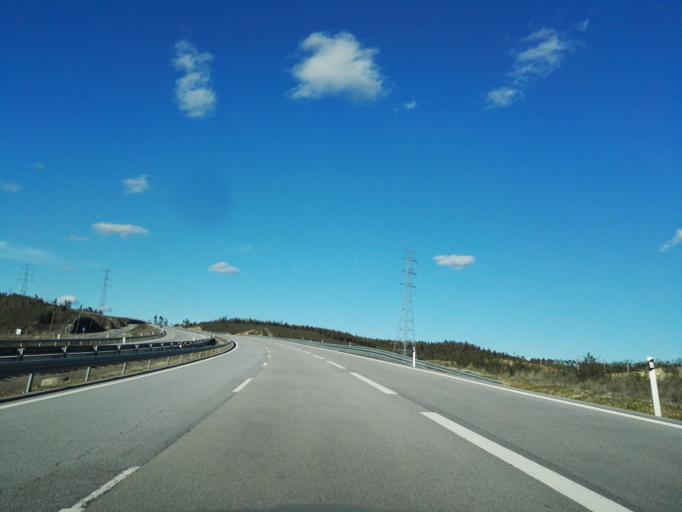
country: PT
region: Portalegre
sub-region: Nisa
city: Nisa
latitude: 39.6027
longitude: -7.7624
